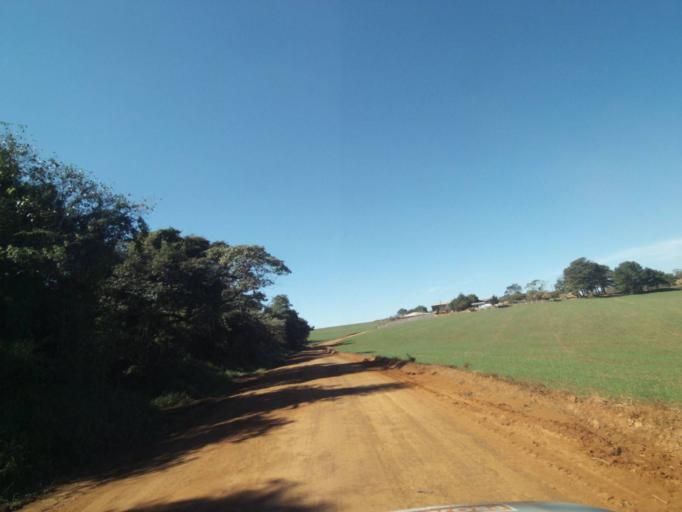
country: BR
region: Parana
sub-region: Tibagi
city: Tibagi
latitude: -24.5796
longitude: -50.6170
